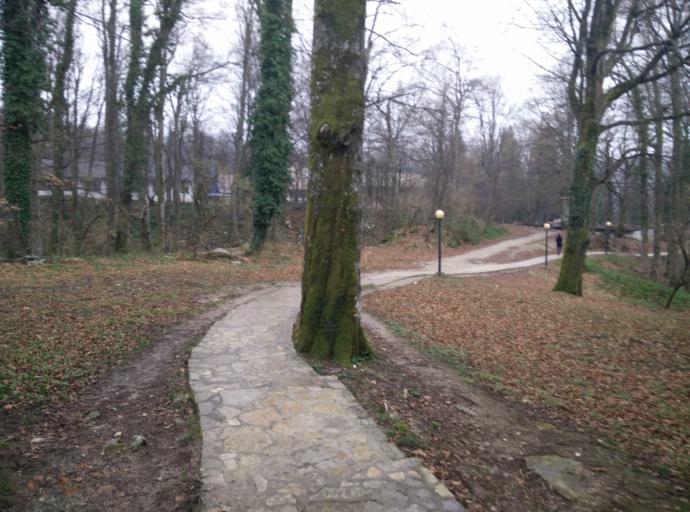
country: HR
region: Licko-Senjska
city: Jezerce
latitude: 44.8835
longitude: 15.6194
